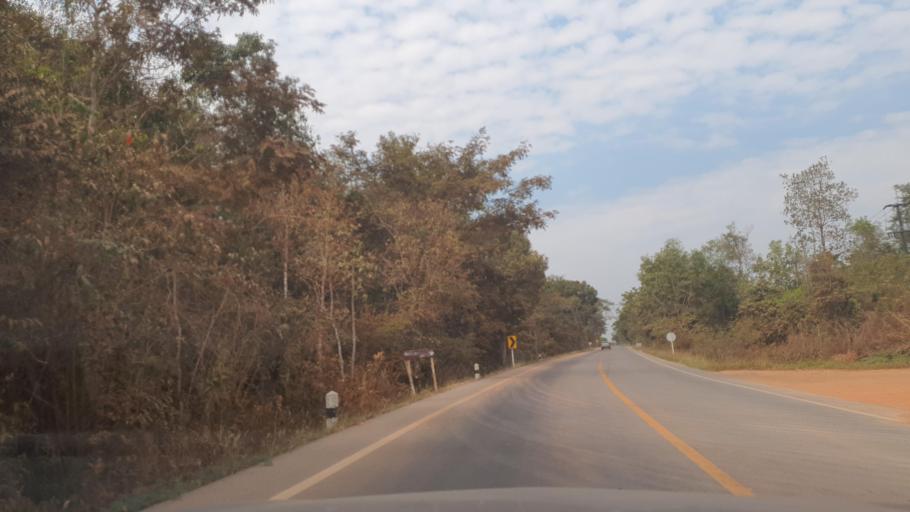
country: TH
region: Changwat Bueng Kan
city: Bung Khla
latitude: 18.2875
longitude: 103.8937
